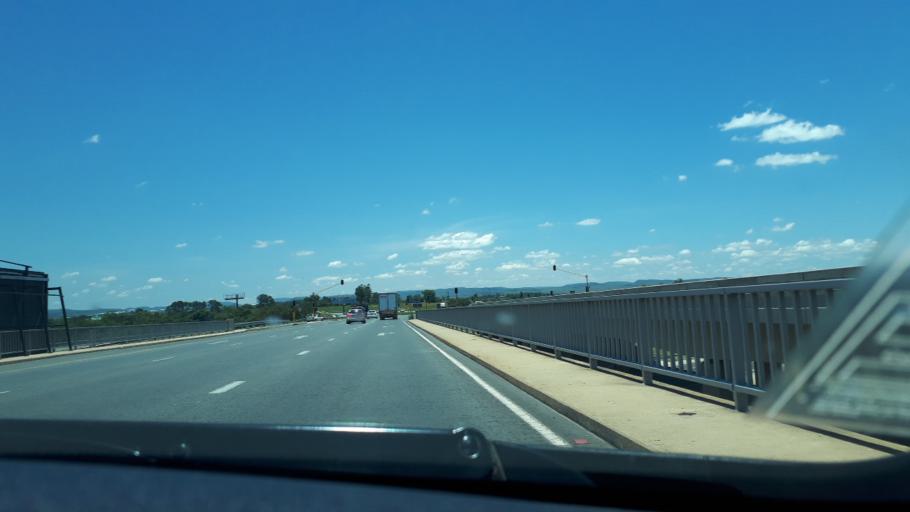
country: ZA
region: Gauteng
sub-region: City of Johannesburg Metropolitan Municipality
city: Diepsloot
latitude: -25.9838
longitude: 27.9253
